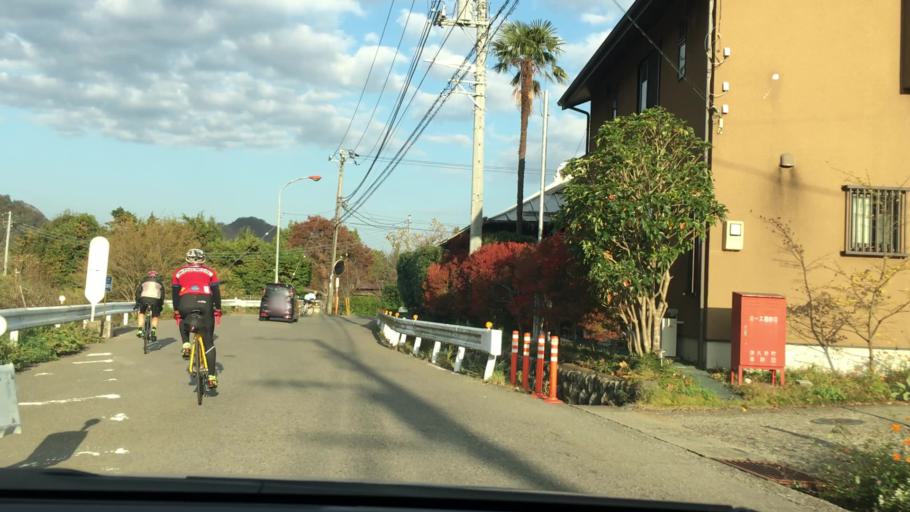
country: JP
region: Yamanashi
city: Uenohara
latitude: 35.5463
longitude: 139.1303
